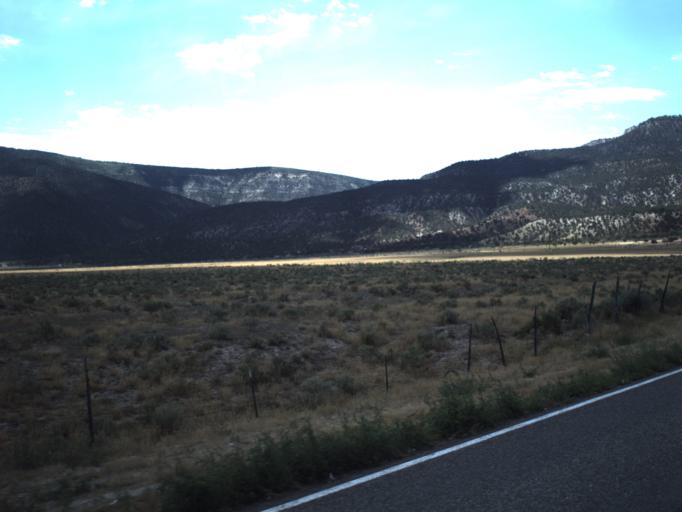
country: US
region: Utah
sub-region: Sanpete County
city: Moroni
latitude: 39.4753
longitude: -111.6310
